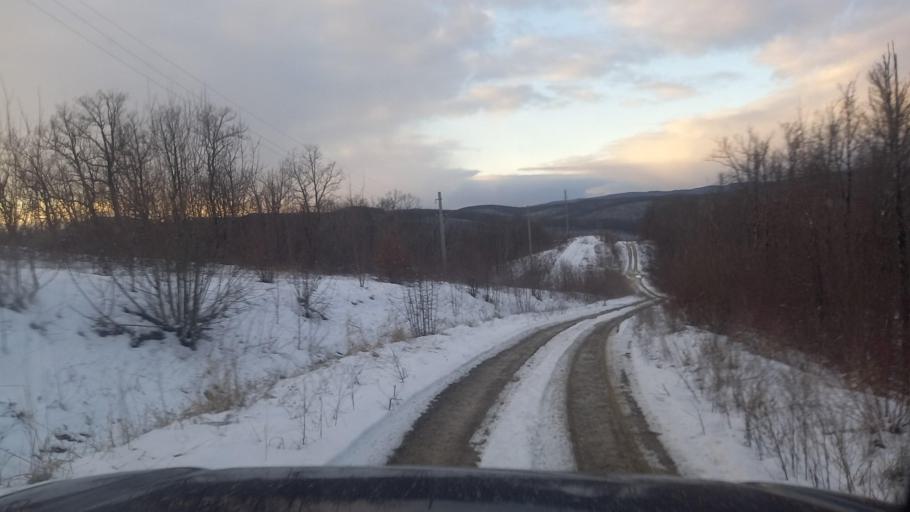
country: RU
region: Krasnodarskiy
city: Smolenskaya
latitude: 44.6756
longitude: 38.7968
